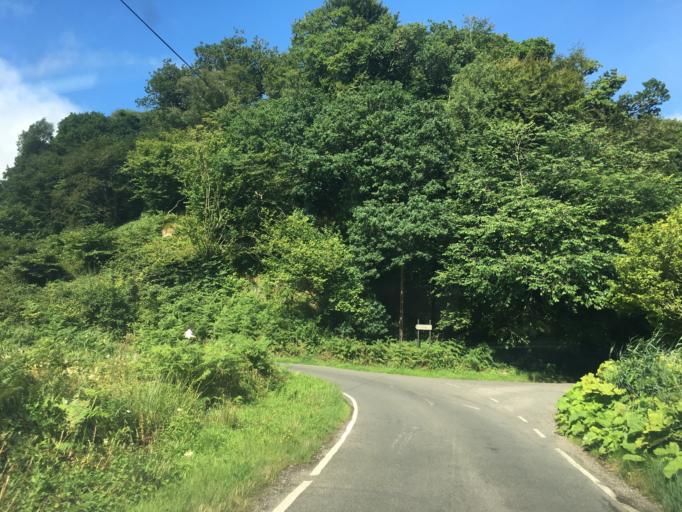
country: GB
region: Scotland
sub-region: Argyll and Bute
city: Ardrishaig
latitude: 56.0825
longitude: -5.5521
